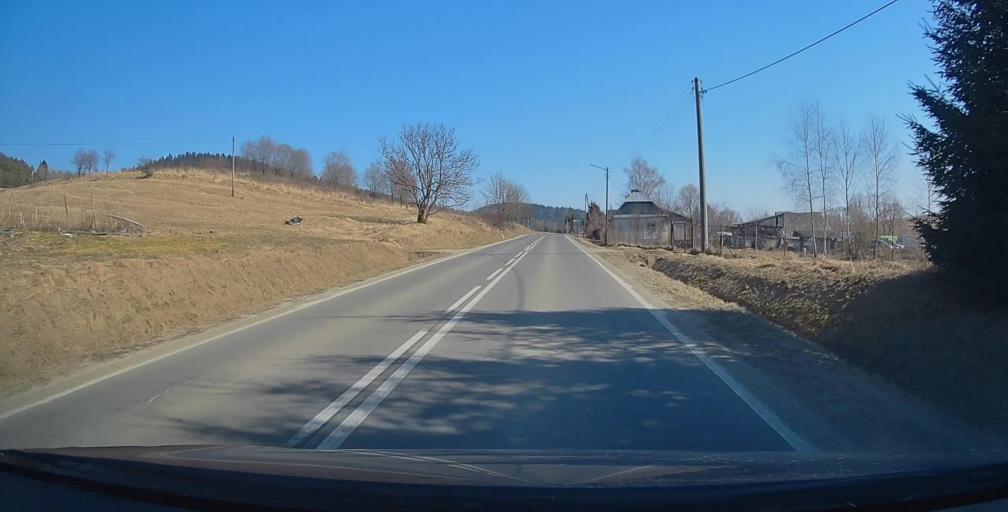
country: PL
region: Subcarpathian Voivodeship
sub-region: Powiat bieszczadzki
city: Ustrzyki Dolne
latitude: 49.4912
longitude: 22.6478
